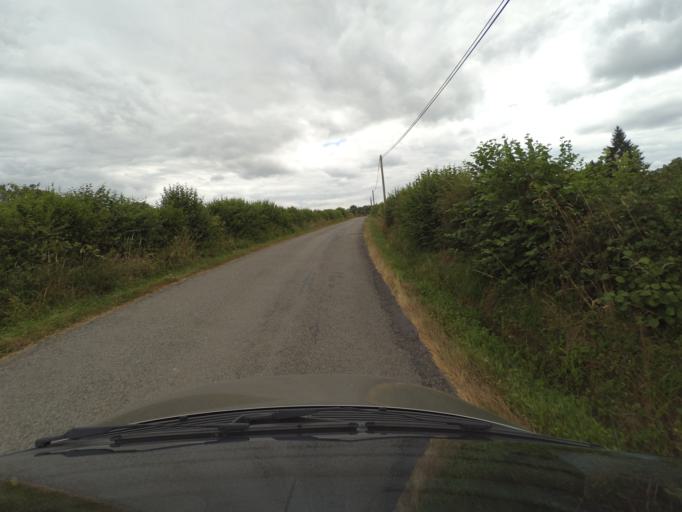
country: FR
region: Limousin
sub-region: Departement de la Haute-Vienne
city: Magnac-Laval
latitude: 46.2817
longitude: 1.2590
